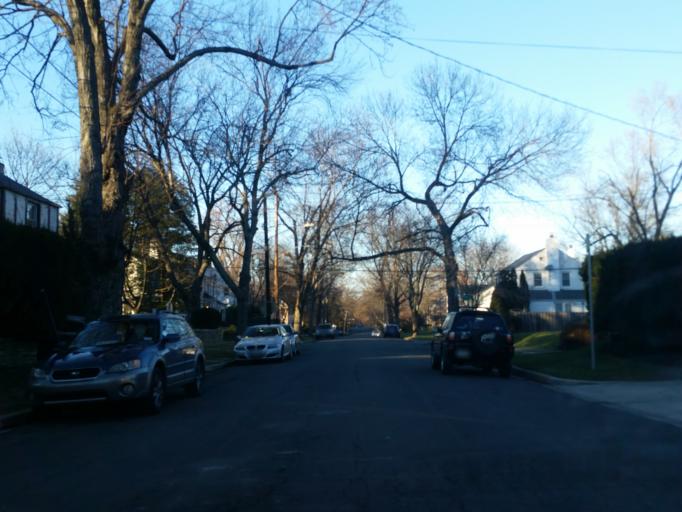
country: US
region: Maryland
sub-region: Montgomery County
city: Friendship Village
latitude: 38.9451
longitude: -77.0926
